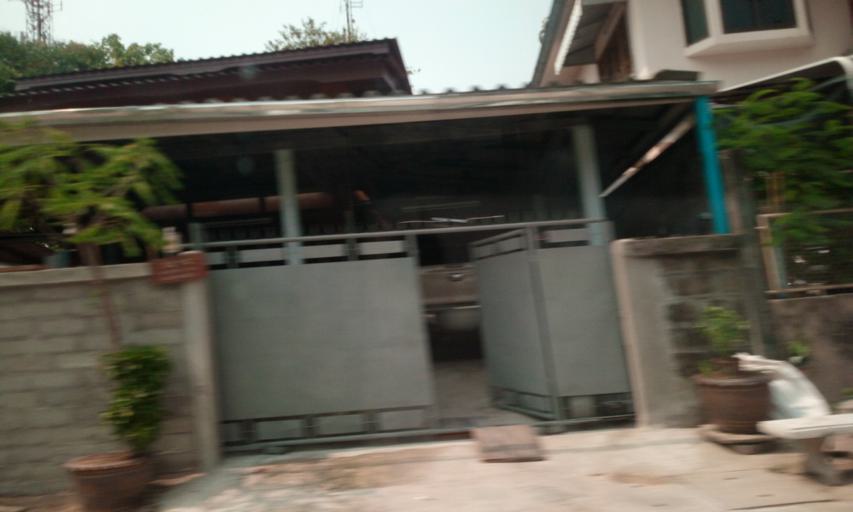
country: TH
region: Chiang Rai
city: Chiang Rai
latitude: 19.9113
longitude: 99.8254
